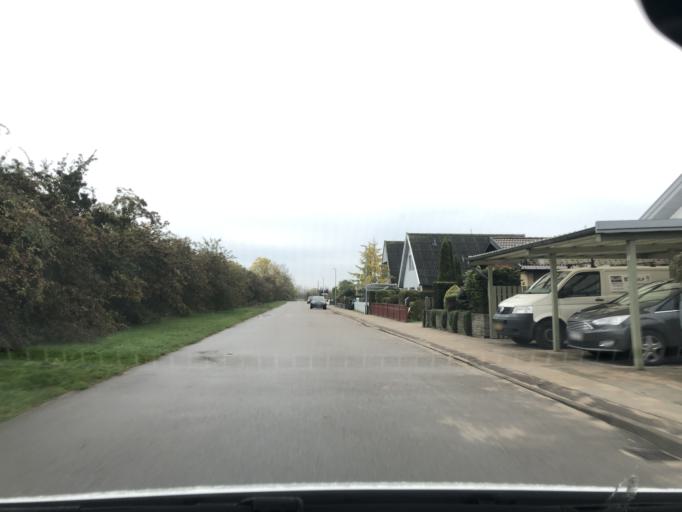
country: DK
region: Capital Region
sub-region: Tarnby Kommune
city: Tarnby
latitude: 55.5938
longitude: 12.5903
